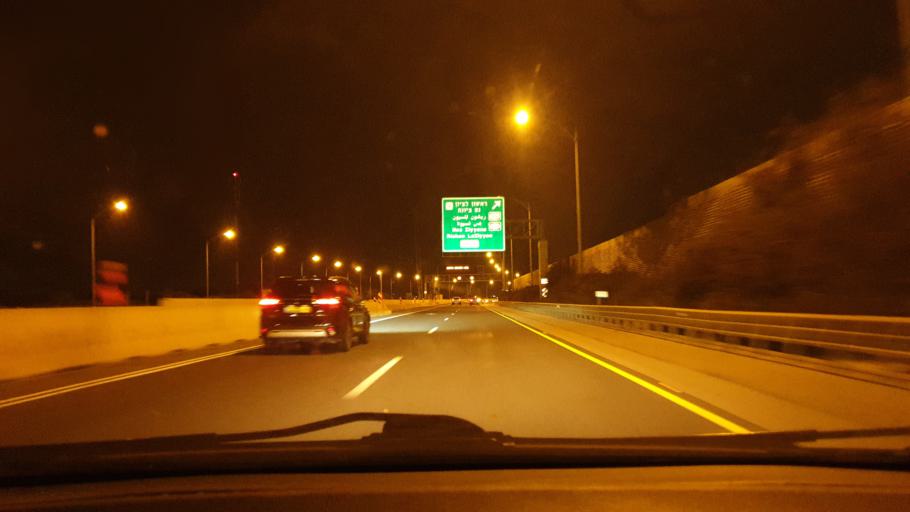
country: IL
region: Central District
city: Ness Ziona
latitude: 31.9313
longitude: 34.8232
